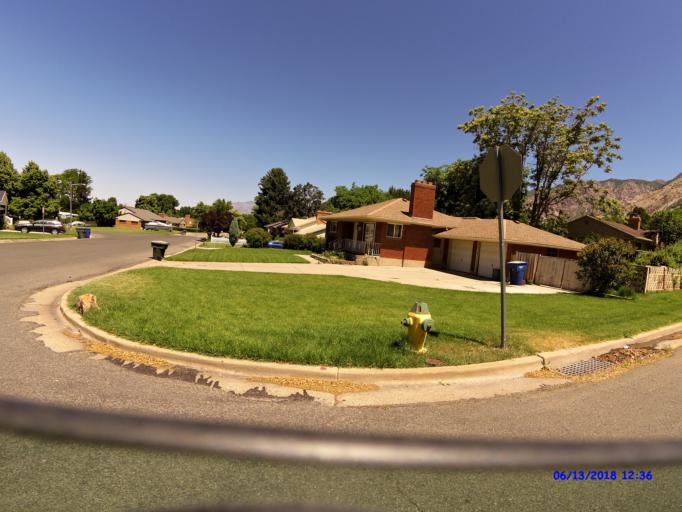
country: US
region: Utah
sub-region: Weber County
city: South Ogden
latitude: 41.1986
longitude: -111.9434
